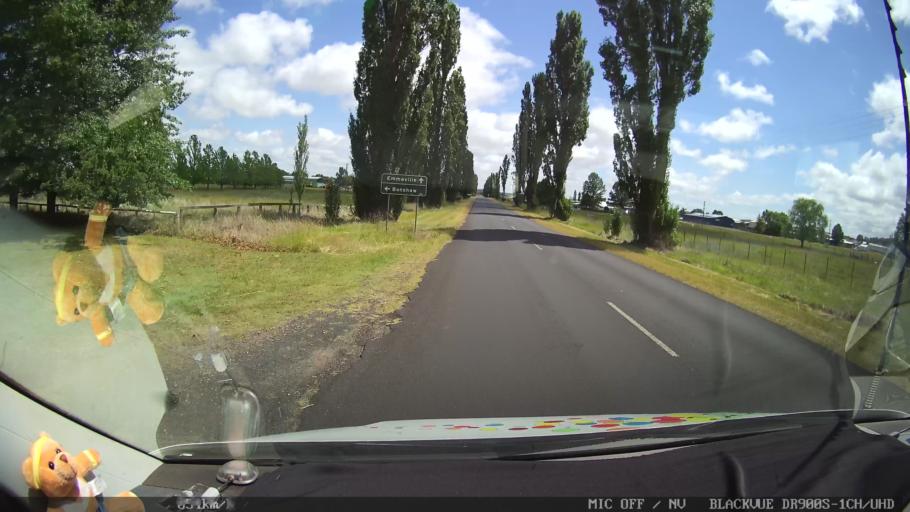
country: AU
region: New South Wales
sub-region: Glen Innes Severn
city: Glen Innes
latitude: -29.7262
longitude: 151.7257
